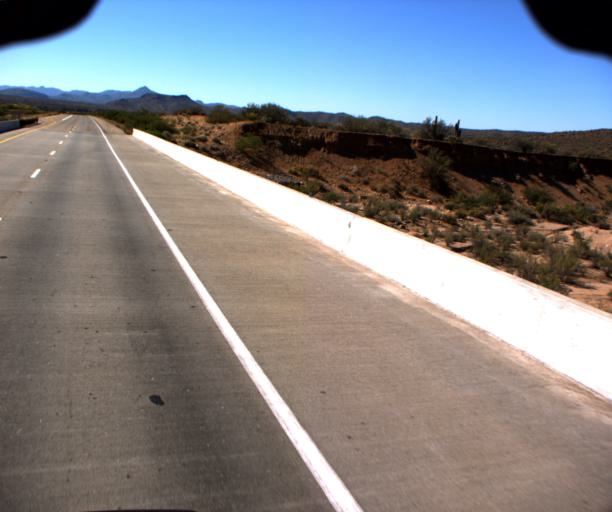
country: US
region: Arizona
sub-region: Yavapai County
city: Bagdad
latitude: 34.6558
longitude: -113.5755
